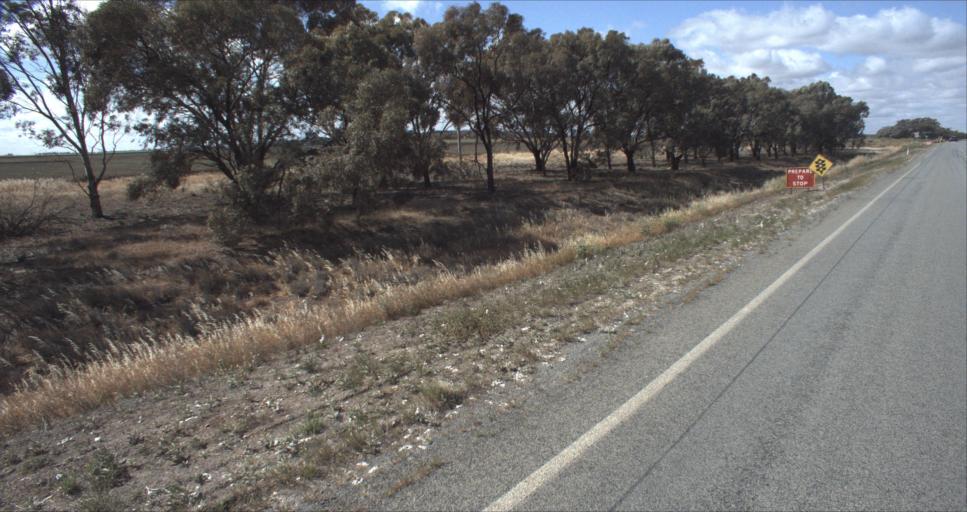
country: AU
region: New South Wales
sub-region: Murrumbidgee Shire
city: Darlington Point
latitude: -34.5508
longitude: 146.1707
